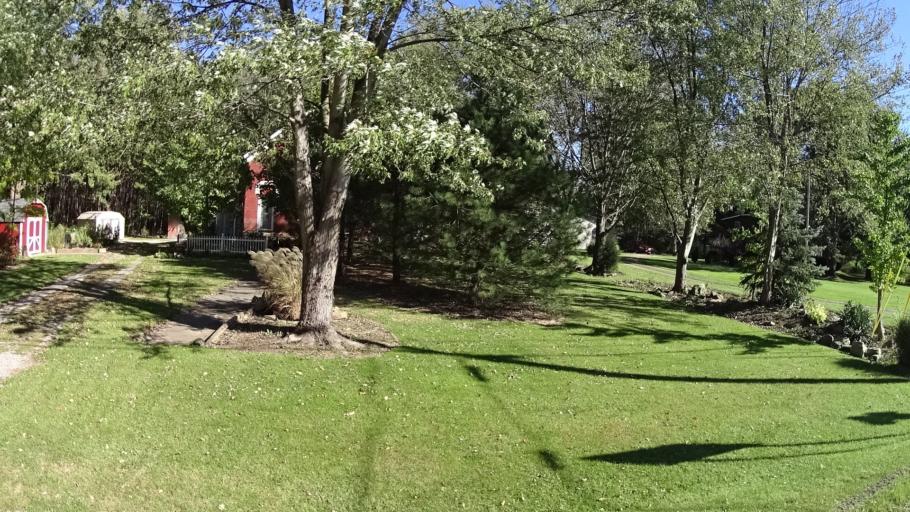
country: US
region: Ohio
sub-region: Lorain County
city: Amherst
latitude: 41.3910
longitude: -82.1648
